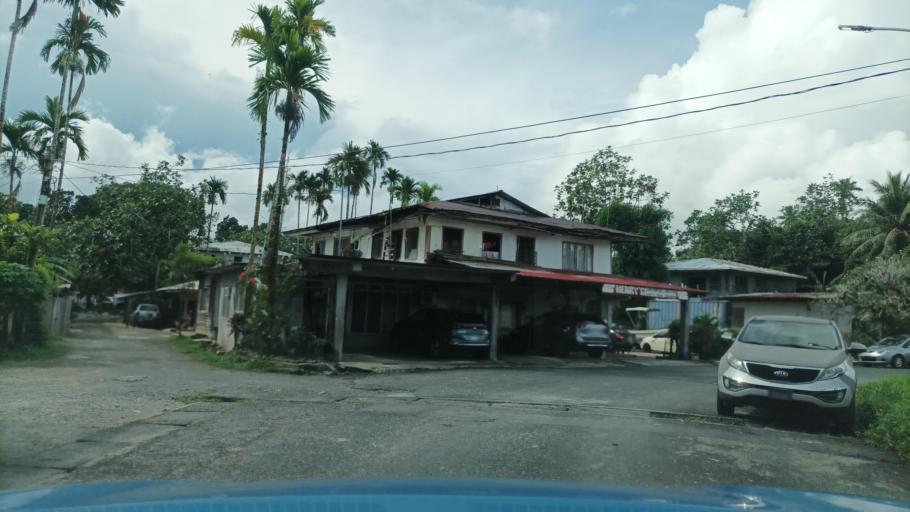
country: FM
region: Pohnpei
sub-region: Kolonia Municipality
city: Kolonia
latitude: 6.9630
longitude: 158.2161
